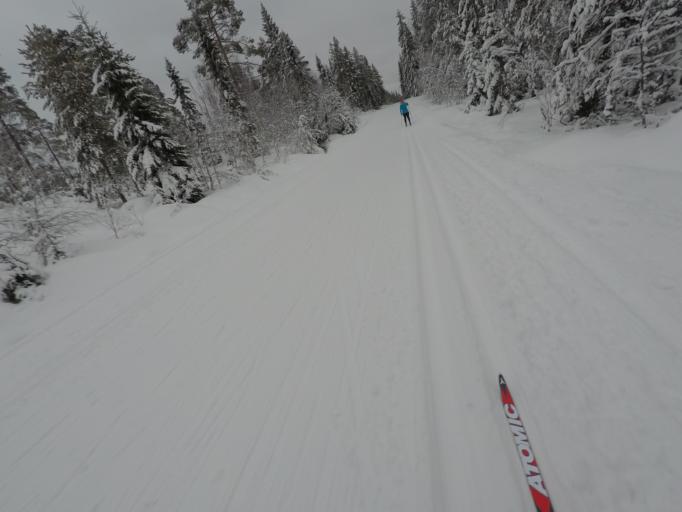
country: SE
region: Dalarna
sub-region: Ludvika Kommun
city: Abborrberget
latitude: 60.1438
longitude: 14.4865
